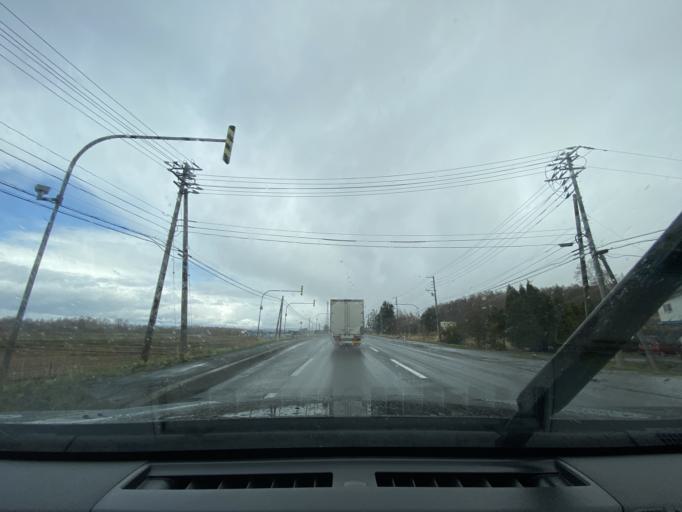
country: JP
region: Hokkaido
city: Fukagawa
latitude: 43.6758
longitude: 142.0263
